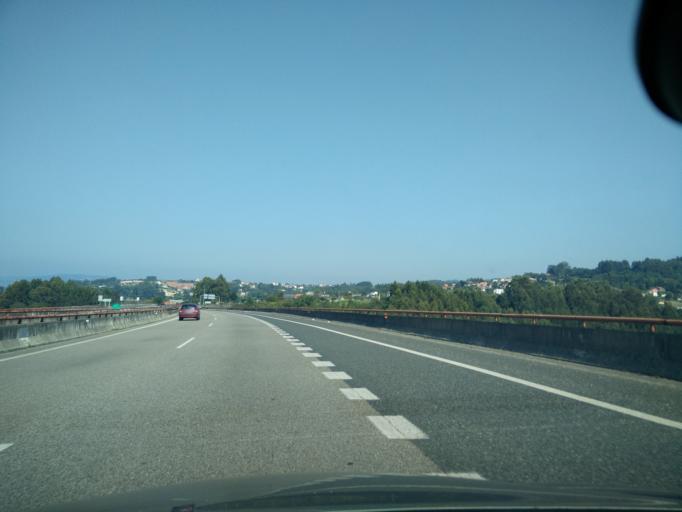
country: ES
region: Galicia
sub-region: Provincia da Coruna
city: Mino
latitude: 43.3513
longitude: -8.2010
